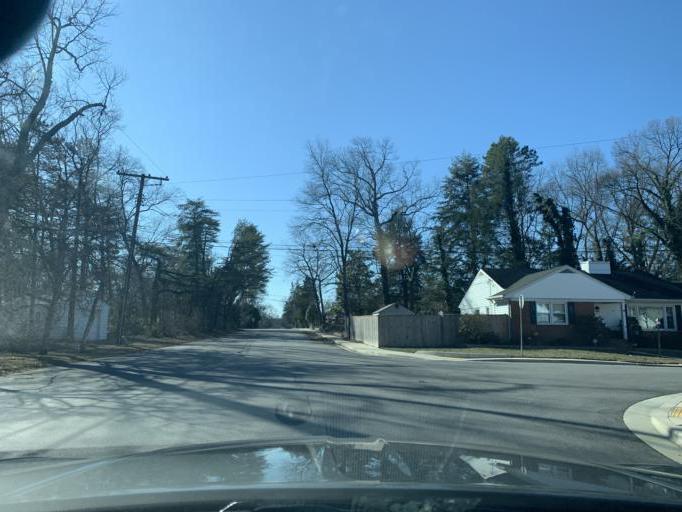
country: US
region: Maryland
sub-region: Anne Arundel County
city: Glen Burnie
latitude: 39.1662
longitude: -76.6315
